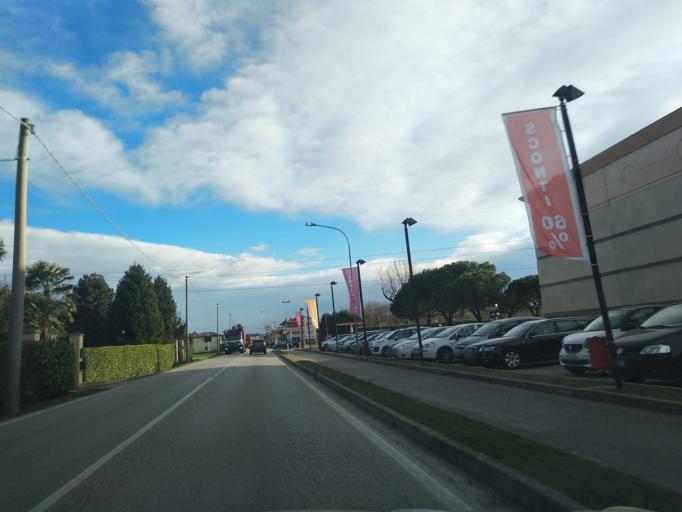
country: IT
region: Veneto
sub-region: Provincia di Vicenza
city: Bolzano Vicentino
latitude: 45.5899
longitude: 11.6240
